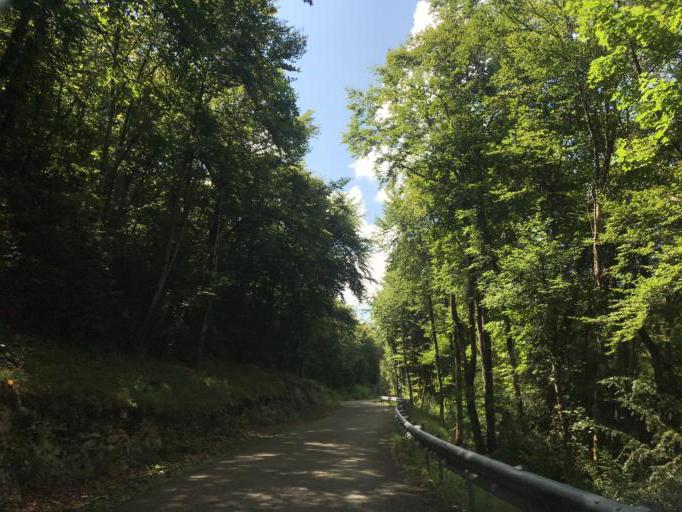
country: FR
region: Franche-Comte
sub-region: Departement du Jura
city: Moirans-en-Montagne
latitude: 46.4975
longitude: 5.7737
